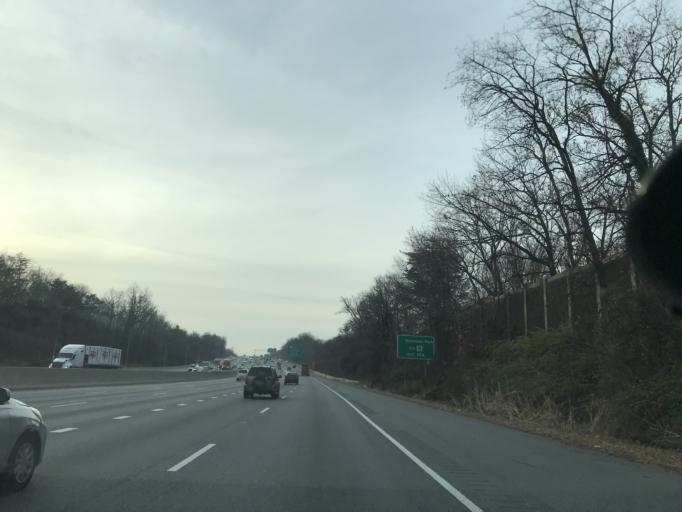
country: US
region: Maryland
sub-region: Prince George's County
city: Glenarden
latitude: 38.9267
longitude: -76.8545
